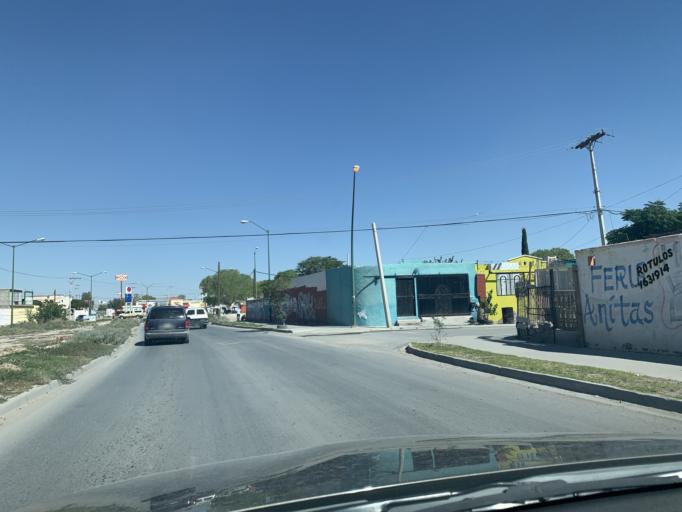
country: US
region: Texas
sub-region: El Paso County
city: Socorro Mission Number 1 Colonia
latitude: 31.5999
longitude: -106.3577
